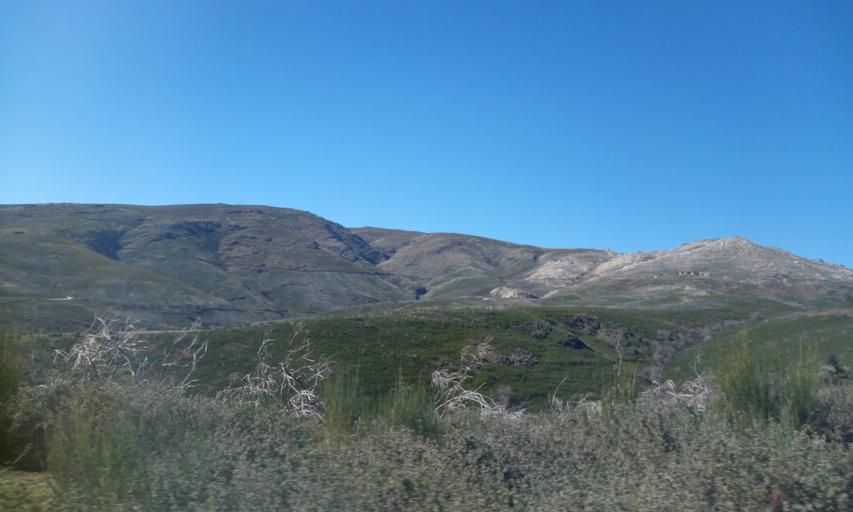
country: PT
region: Guarda
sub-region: Manteigas
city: Manteigas
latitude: 40.4677
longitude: -7.5028
